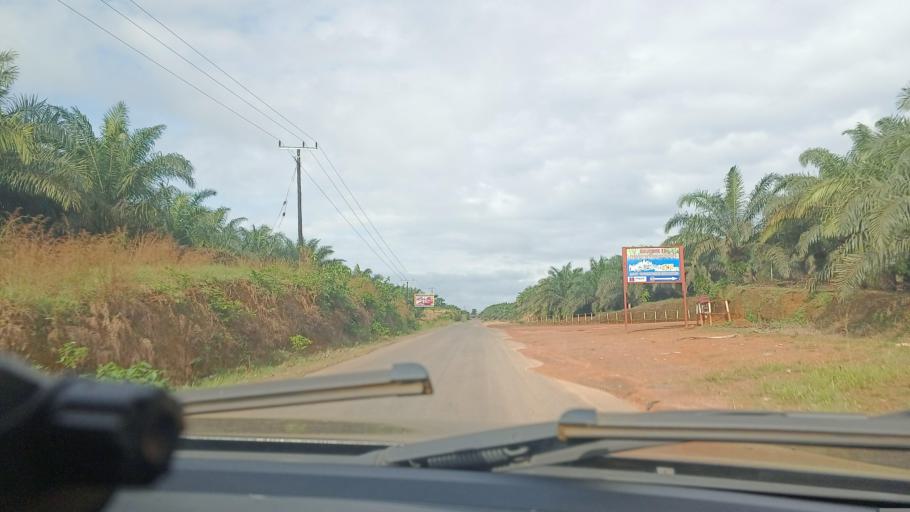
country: LR
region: Bomi
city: Tubmanburg
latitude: 6.7123
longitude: -10.9605
